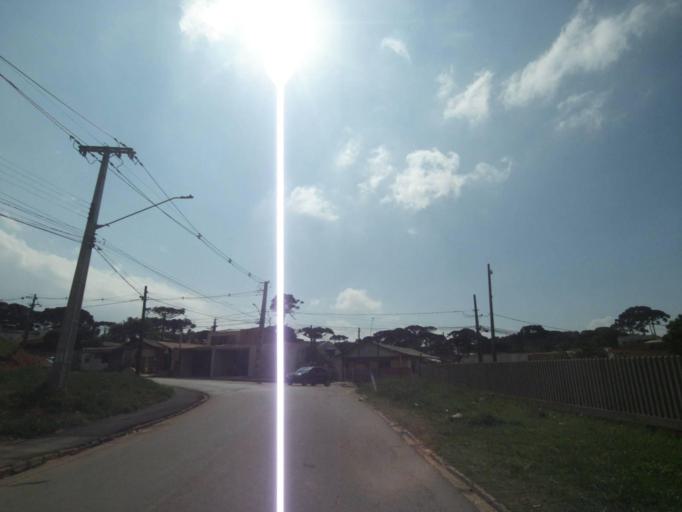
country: BR
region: Parana
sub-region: Araucaria
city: Araucaria
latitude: -25.5049
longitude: -49.3487
